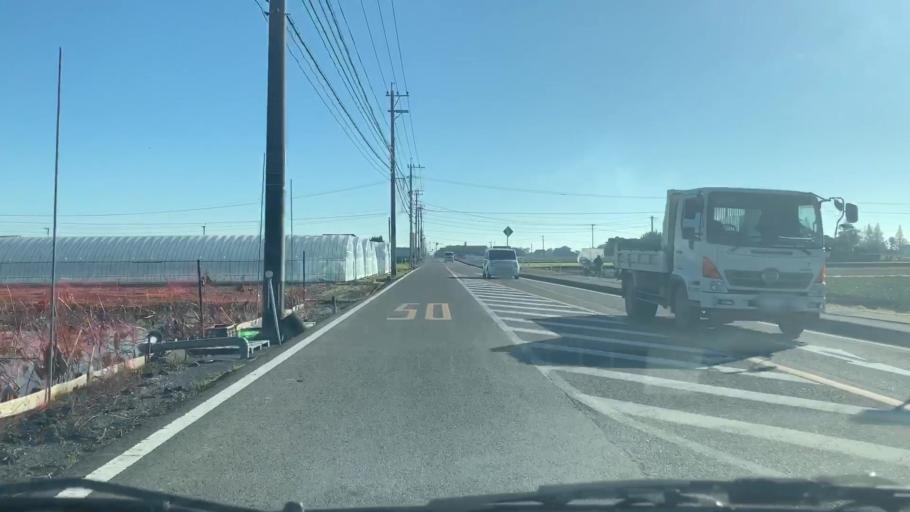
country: JP
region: Saga Prefecture
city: Kashima
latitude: 33.1848
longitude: 130.1583
